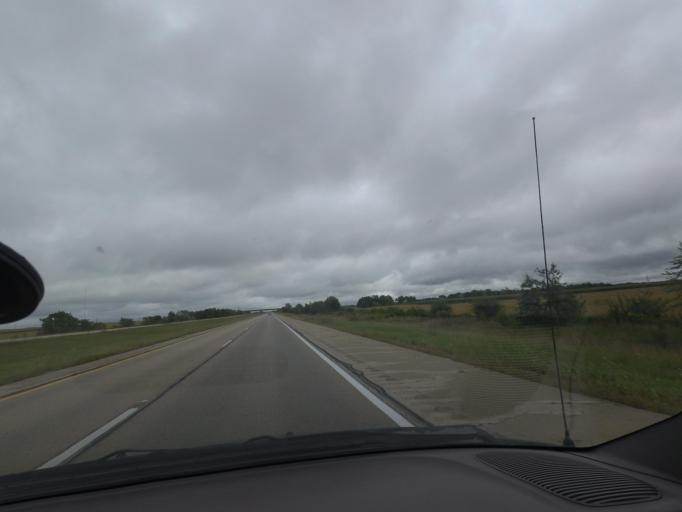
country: US
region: Illinois
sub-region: Piatt County
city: Monticello
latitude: 40.0223
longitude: -88.6958
